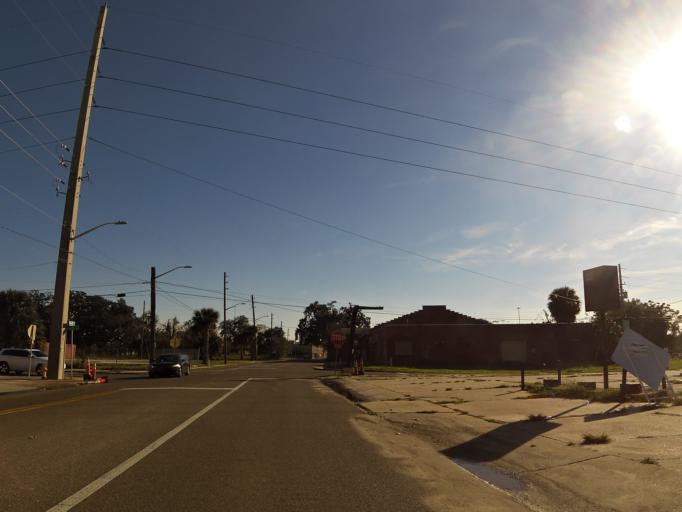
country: US
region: Florida
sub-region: Duval County
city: Jacksonville
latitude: 30.3340
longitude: -81.6760
